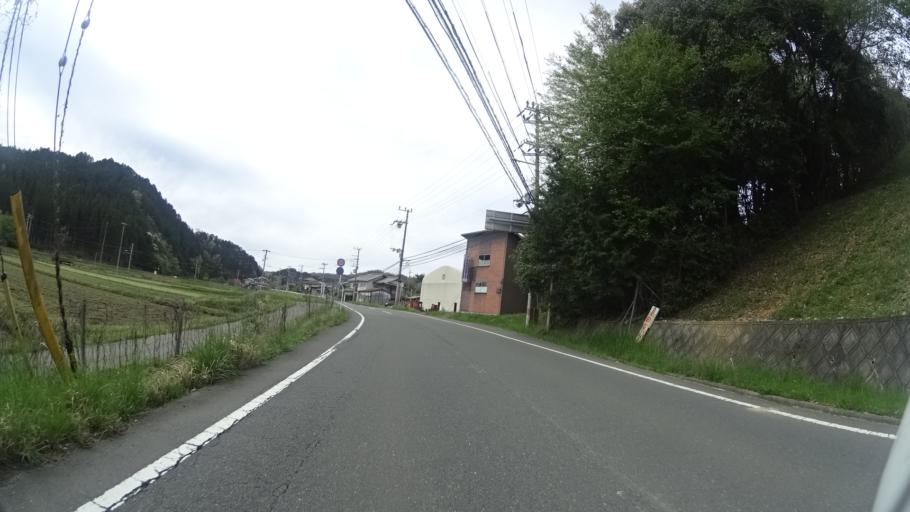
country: JP
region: Kyoto
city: Kameoka
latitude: 35.1899
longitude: 135.4825
